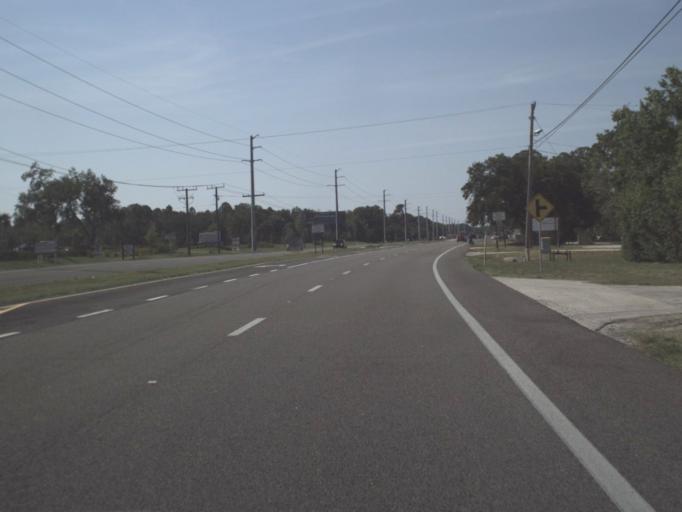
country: US
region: Florida
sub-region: Brevard County
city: Port Saint John
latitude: 28.4954
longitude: -80.7796
